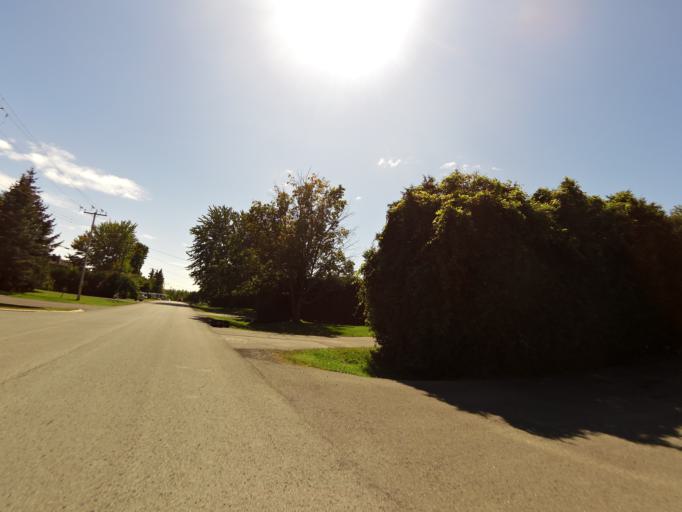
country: CA
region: Ontario
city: Bells Corners
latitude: 45.1896
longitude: -75.8253
